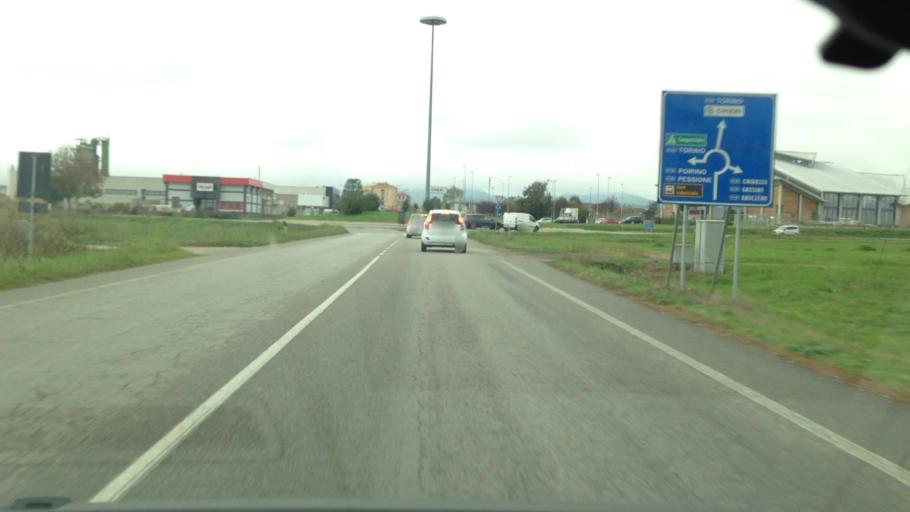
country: IT
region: Piedmont
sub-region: Provincia di Torino
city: Riva Presso Chieri
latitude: 44.9994
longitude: 7.8487
